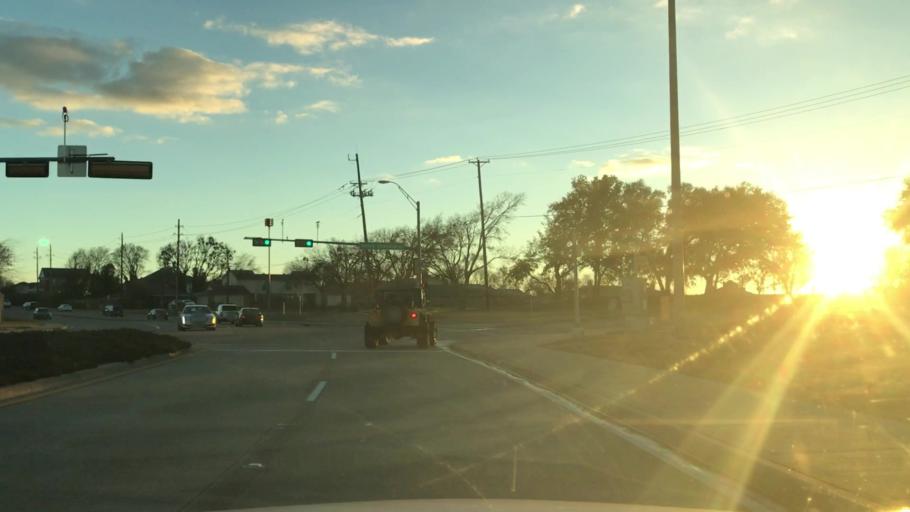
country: US
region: Texas
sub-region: Rockwall County
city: Heath
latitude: 32.8761
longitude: -96.4745
